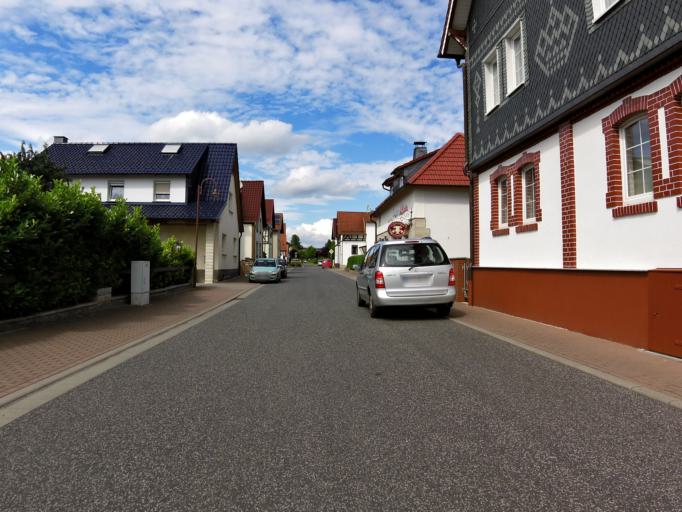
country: DE
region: Thuringia
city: Dorndorf
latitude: 50.8430
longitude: 10.1230
